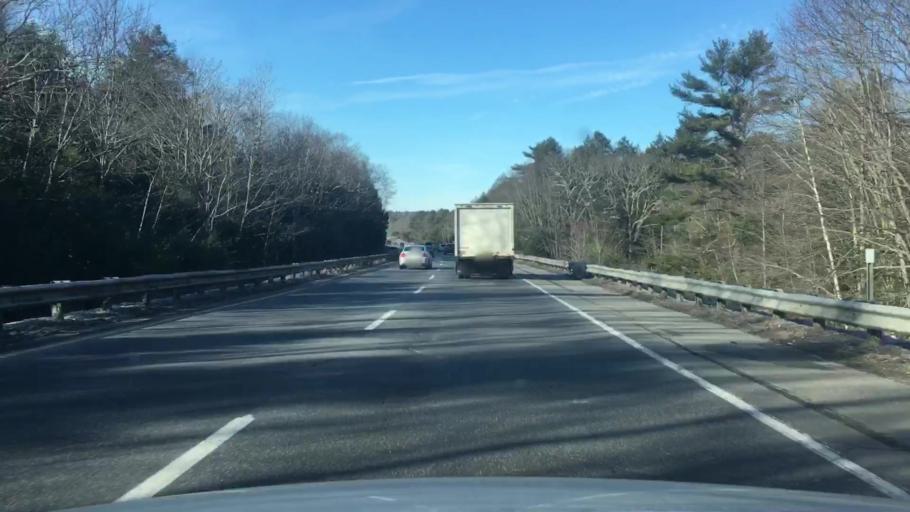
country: US
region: Maine
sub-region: Sagadahoc County
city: Bath
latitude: 43.9146
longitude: -69.8496
